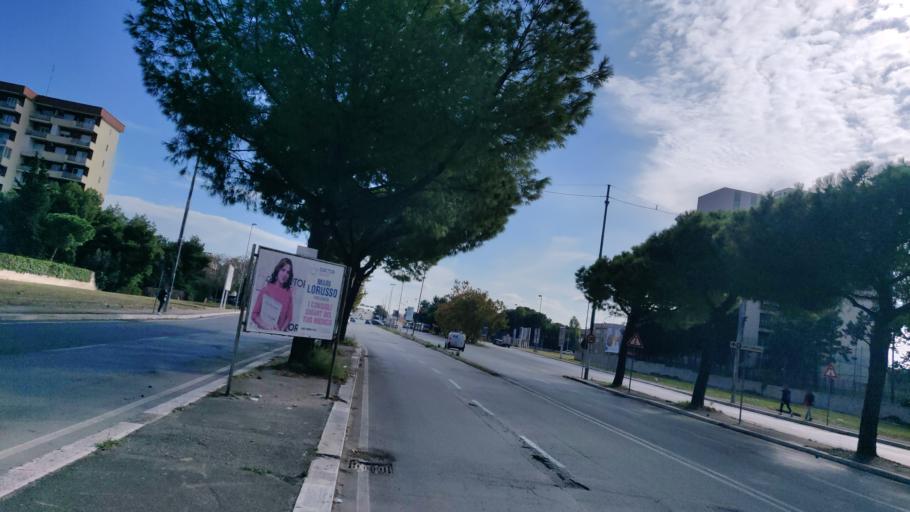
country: IT
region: Apulia
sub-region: Provincia di Bari
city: Triggiano
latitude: 41.1036
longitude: 16.9065
